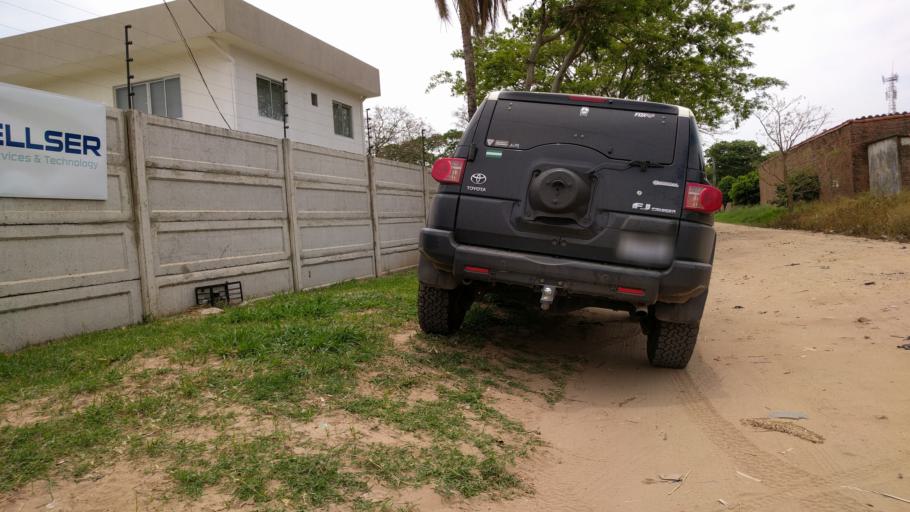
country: BO
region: Santa Cruz
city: Santa Cruz de la Sierra
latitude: -17.8150
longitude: -63.2324
